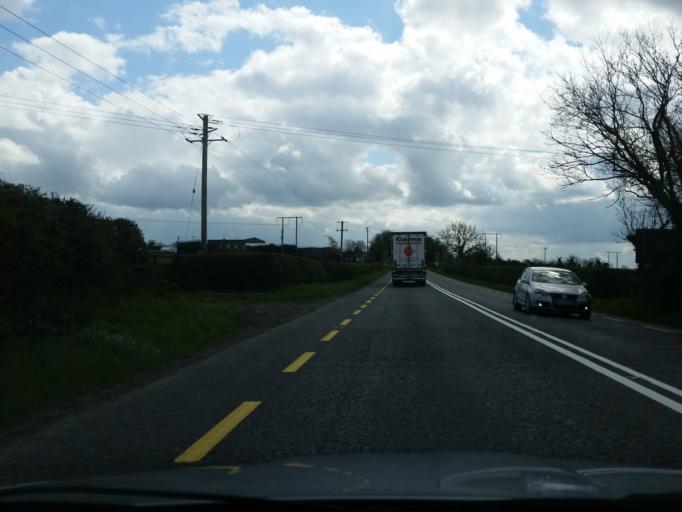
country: IE
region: Leinster
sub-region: An Mhi
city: Ratoath
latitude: 53.5560
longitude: -6.4385
